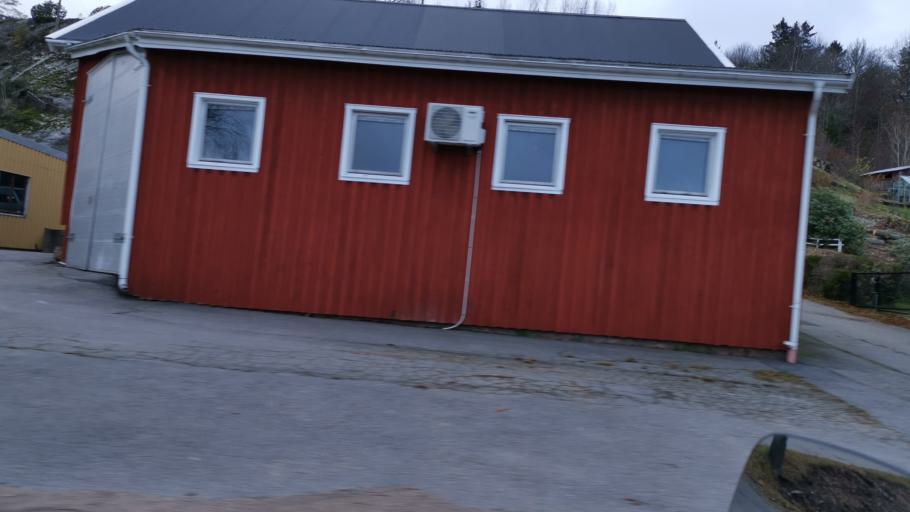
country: SE
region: Vaestra Goetaland
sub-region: Orust
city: Henan
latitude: 58.2579
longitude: 11.7294
